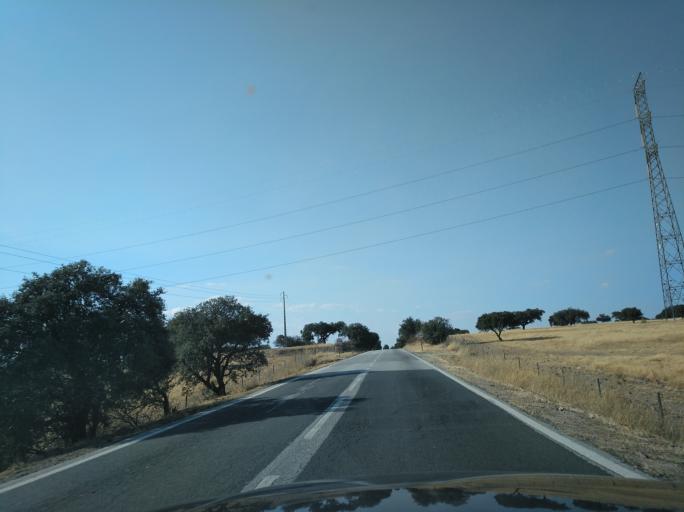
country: ES
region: Extremadura
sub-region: Provincia de Badajoz
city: Valencia del Mombuey
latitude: 38.2425
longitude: -7.2387
